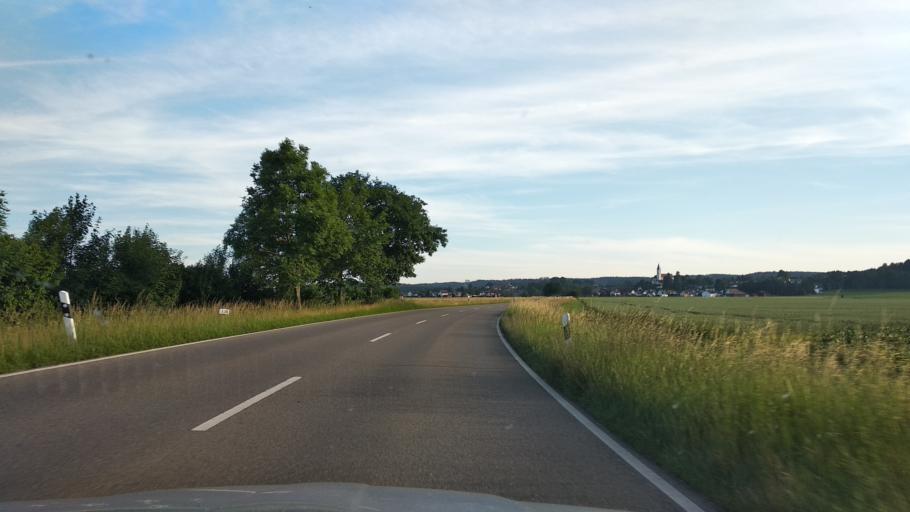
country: DE
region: Baden-Wuerttemberg
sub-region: Tuebingen Region
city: Kirchberg an der Iller
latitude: 48.1428
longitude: 10.0910
